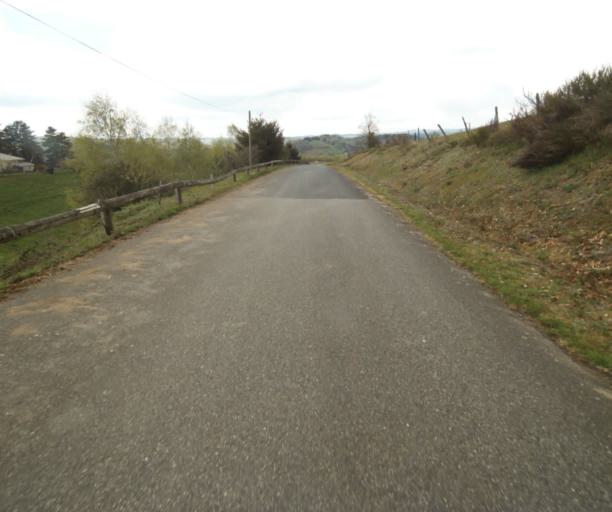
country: FR
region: Limousin
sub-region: Departement de la Correze
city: Naves
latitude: 45.3092
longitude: 1.8116
